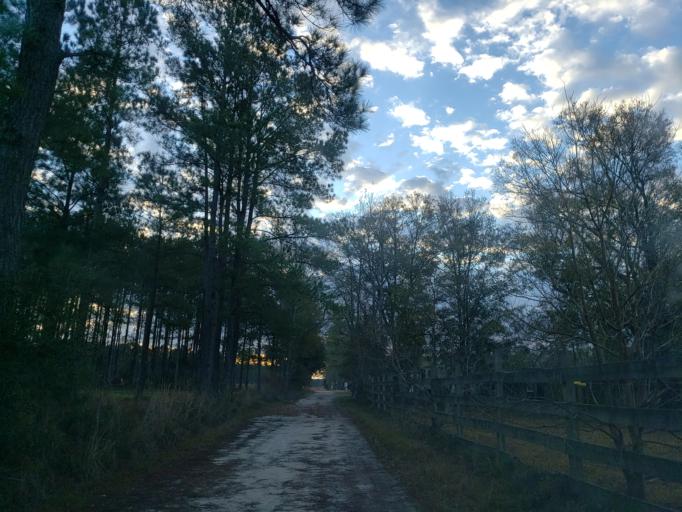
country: US
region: Georgia
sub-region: Chatham County
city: Bloomingdale
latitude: 32.1126
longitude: -81.3440
